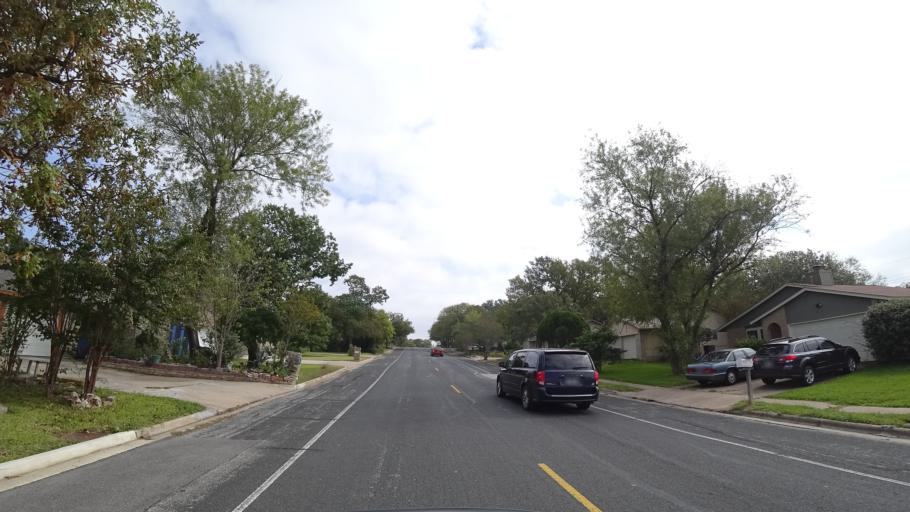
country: US
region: Texas
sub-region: Travis County
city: Shady Hollow
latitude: 30.1988
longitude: -97.8324
